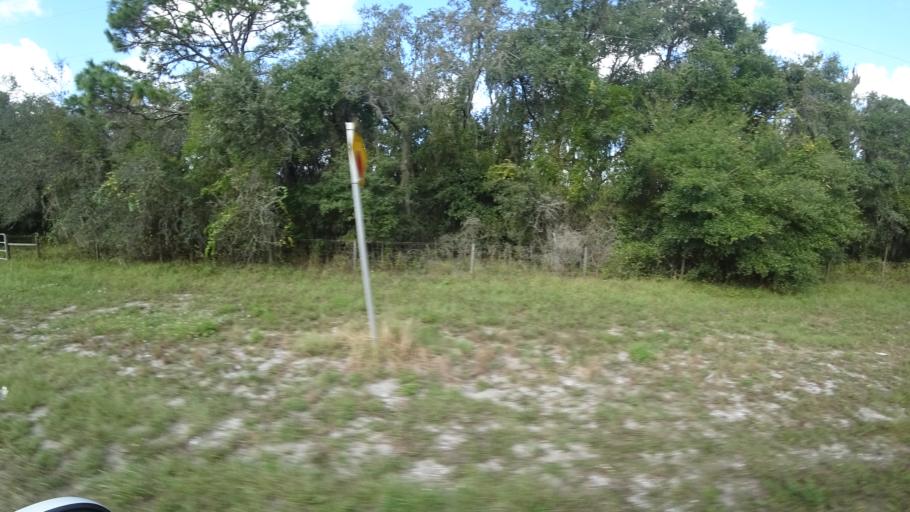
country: US
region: Florida
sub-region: Sarasota County
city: The Meadows
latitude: 27.4784
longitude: -82.2990
